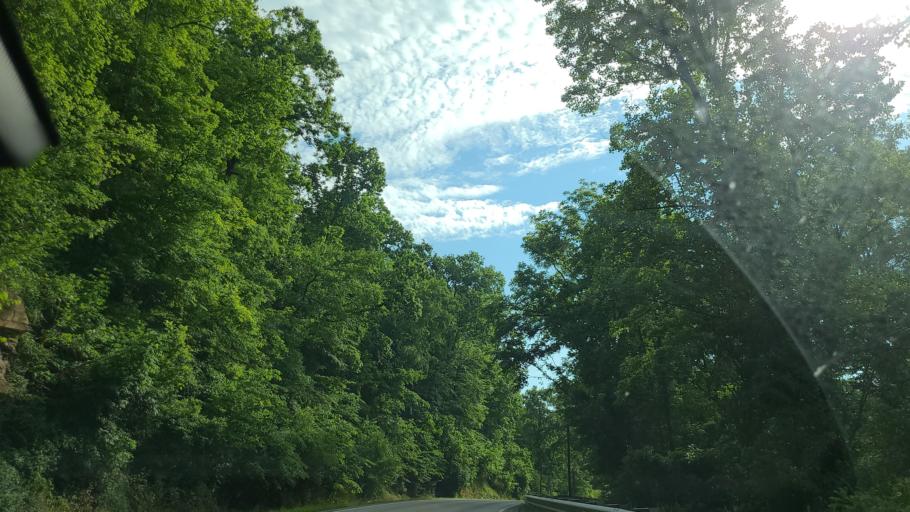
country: US
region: Kentucky
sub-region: Whitley County
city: Williamsburg
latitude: 36.7300
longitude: -84.1239
